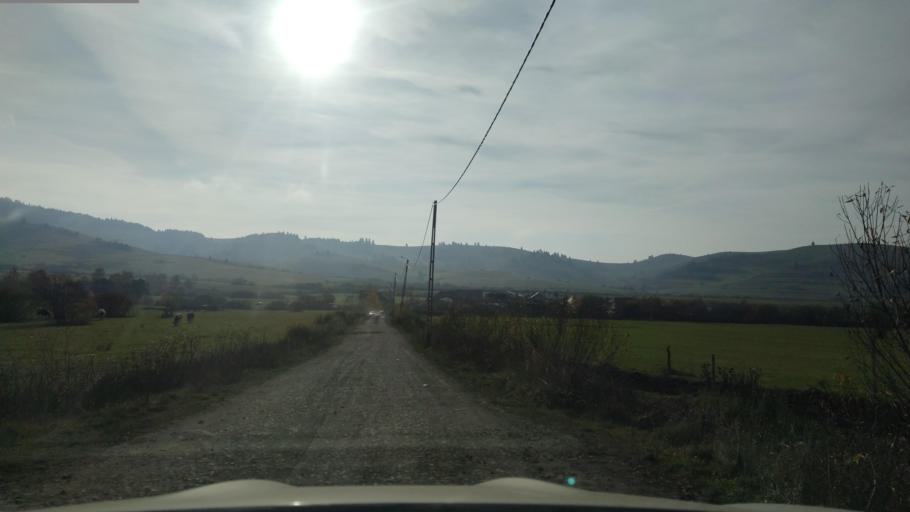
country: RO
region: Harghita
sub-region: Comuna Ditrau
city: Ditrau
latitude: 46.8239
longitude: 25.5353
